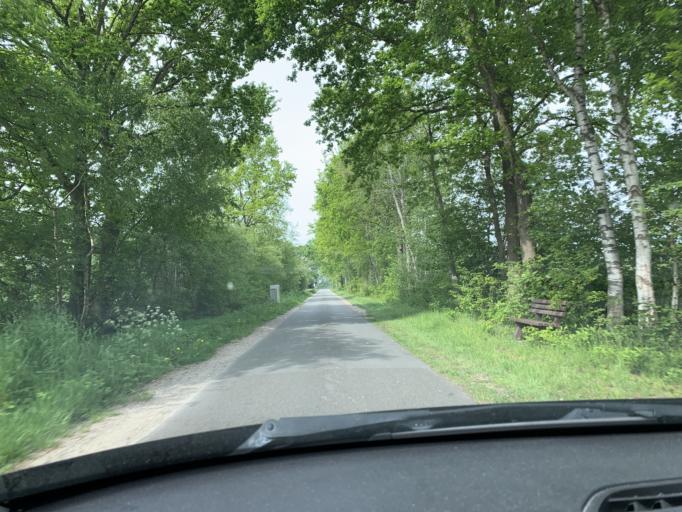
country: DE
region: Lower Saxony
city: Apen
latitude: 53.2094
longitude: 7.7644
